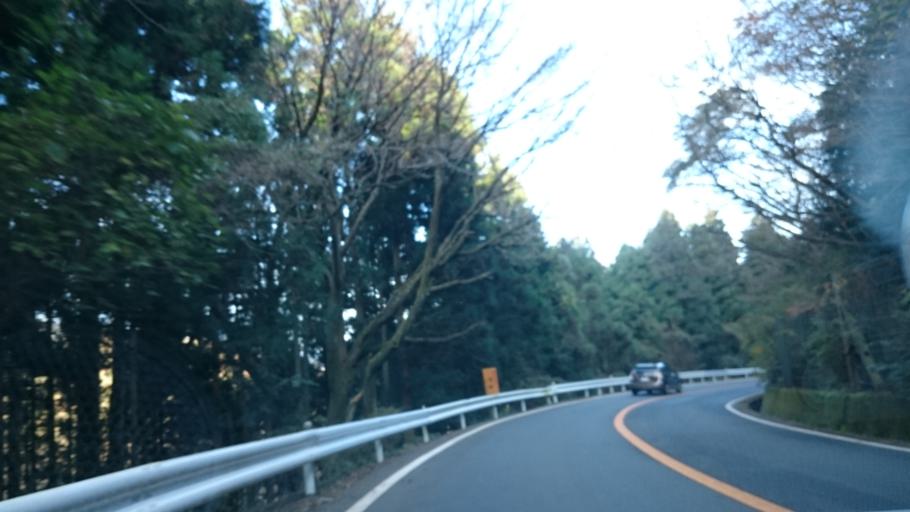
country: JP
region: Shizuoka
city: Heda
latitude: 34.9744
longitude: 138.8627
